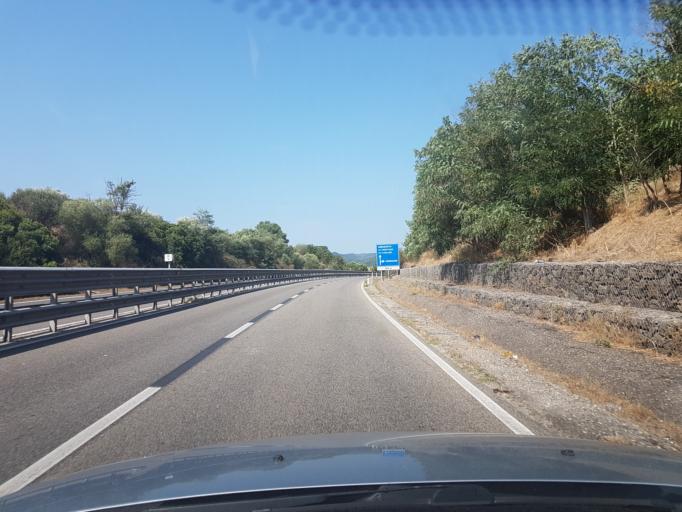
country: IT
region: Sardinia
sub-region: Provincia di Oristano
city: Soddi
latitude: 40.1489
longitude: 8.8933
